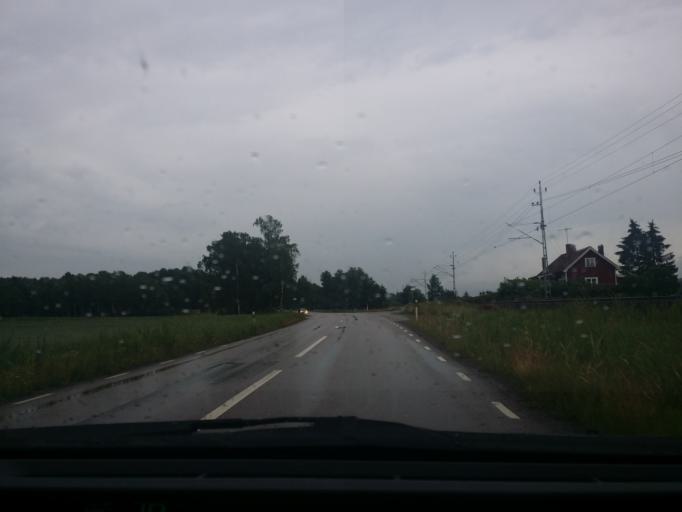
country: SE
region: Vaestmanland
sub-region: Arboga Kommun
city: Arboga
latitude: 59.4136
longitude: 15.7533
